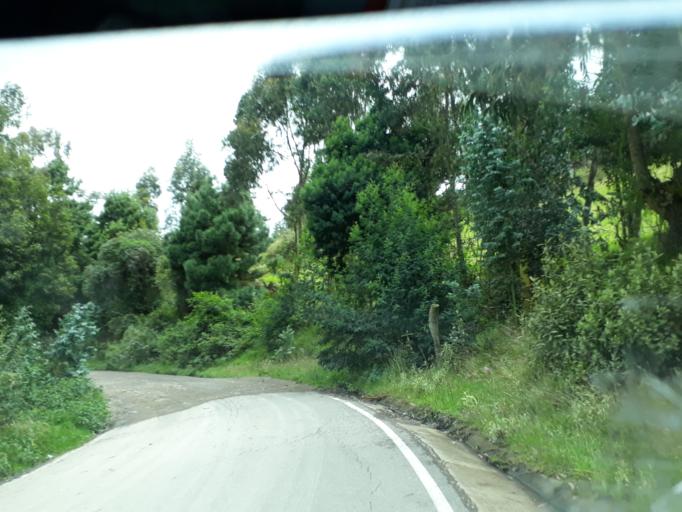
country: CO
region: Cundinamarca
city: Sutatausa
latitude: 5.1990
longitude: -73.8980
